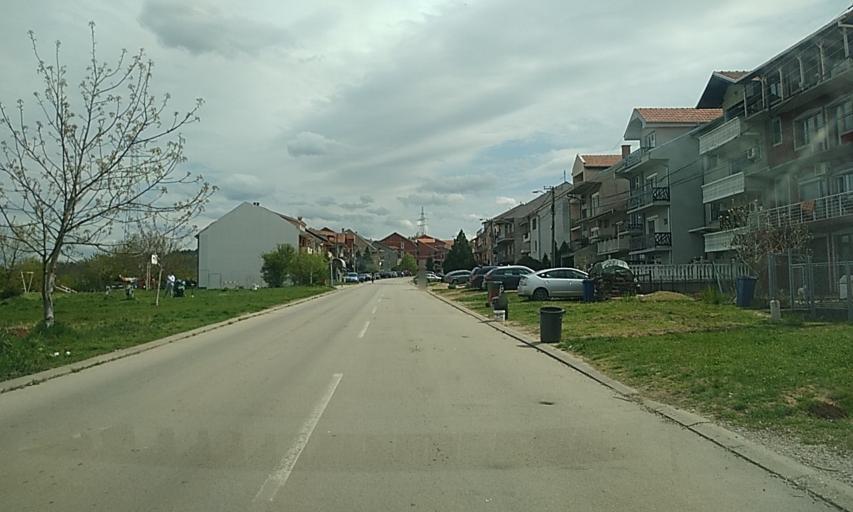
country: RS
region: Central Serbia
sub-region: Nisavski Okrug
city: Nis
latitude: 43.3098
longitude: 21.8635
